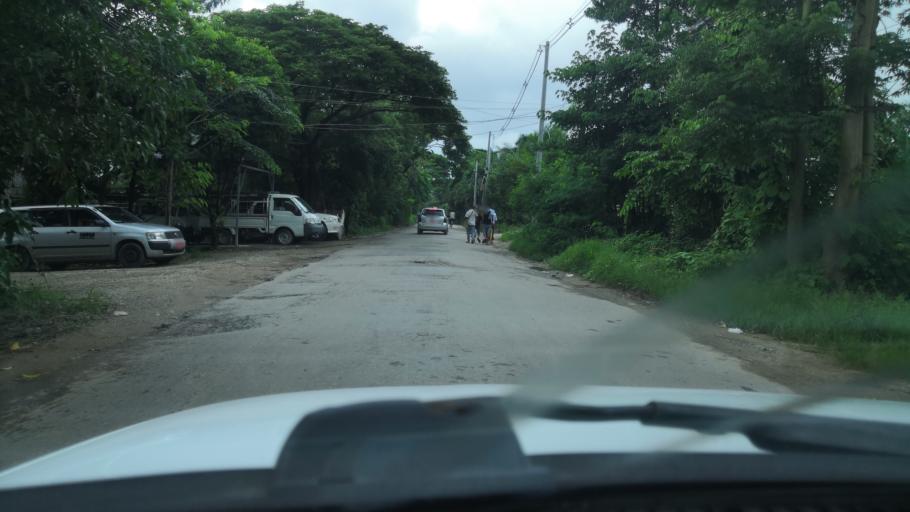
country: MM
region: Yangon
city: Yangon
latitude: 16.8804
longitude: 96.1798
